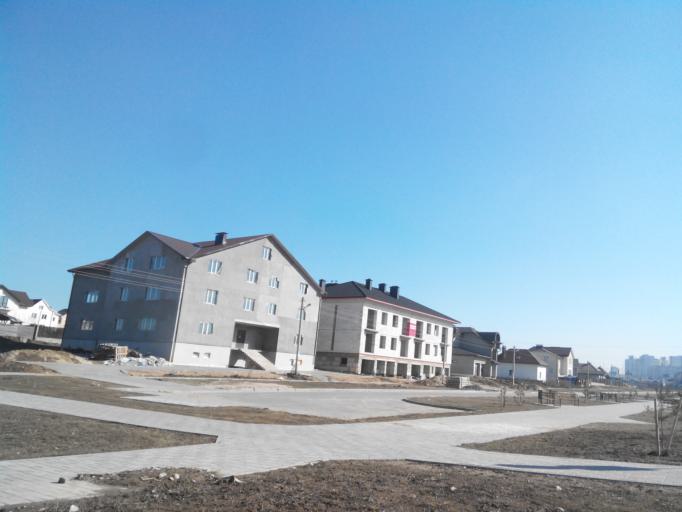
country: BY
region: Minsk
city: Zhdanovichy
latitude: 53.9189
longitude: 27.4062
